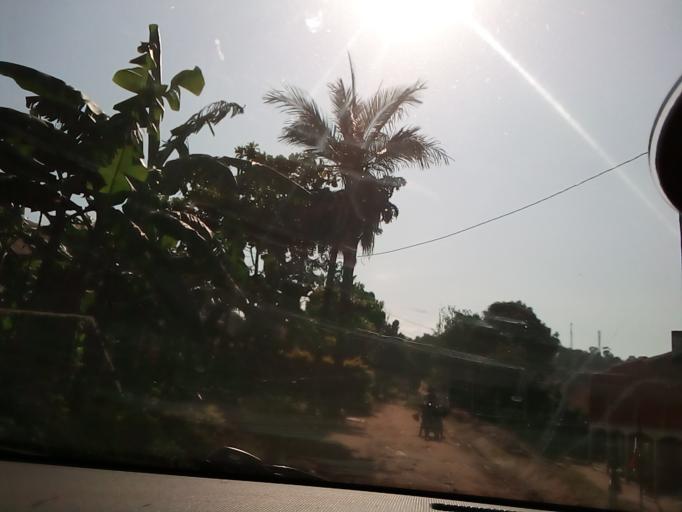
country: UG
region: Central Region
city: Masaka
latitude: -0.3387
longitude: 31.7271
